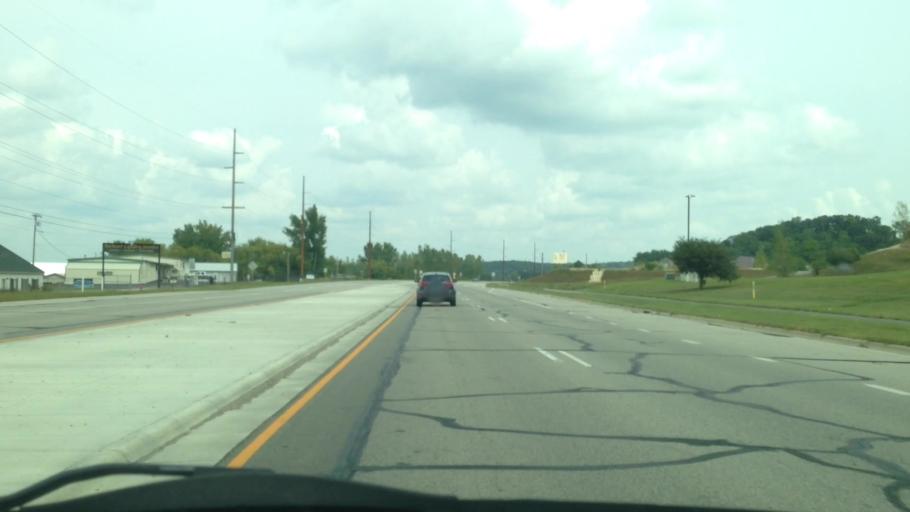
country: US
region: Minnesota
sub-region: Olmsted County
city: Rochester
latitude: 44.0602
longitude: -92.4533
